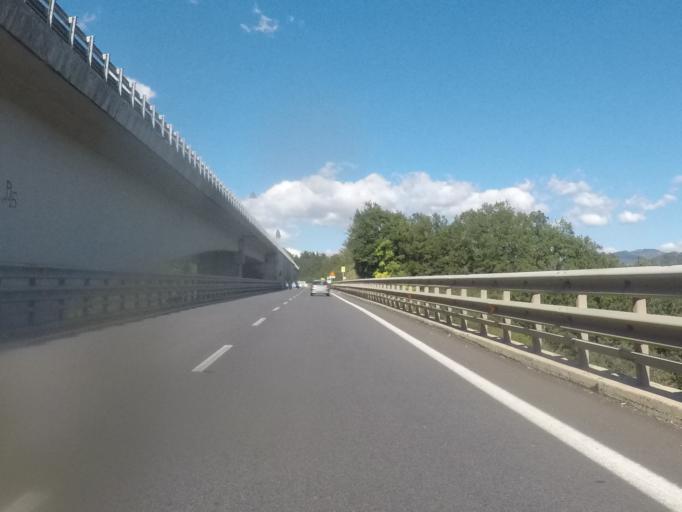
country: IT
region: Calabria
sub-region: Provincia di Cosenza
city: Altilia
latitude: 39.1366
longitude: 16.2731
